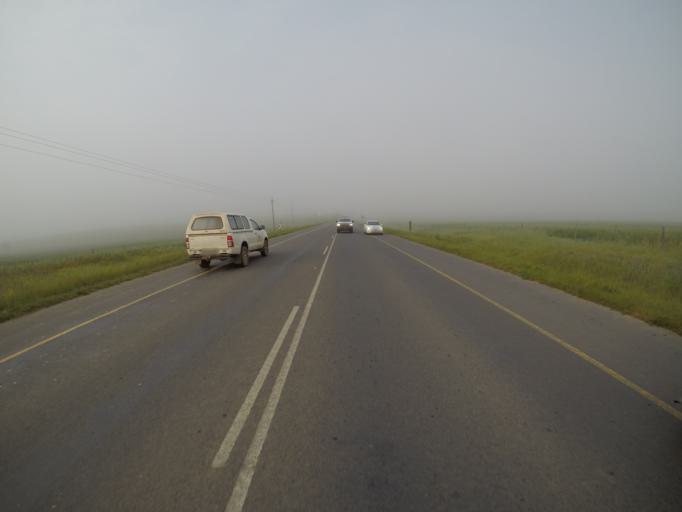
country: ZA
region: Western Cape
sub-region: City of Cape Town
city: Kraaifontein
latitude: -33.7816
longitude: 18.7051
